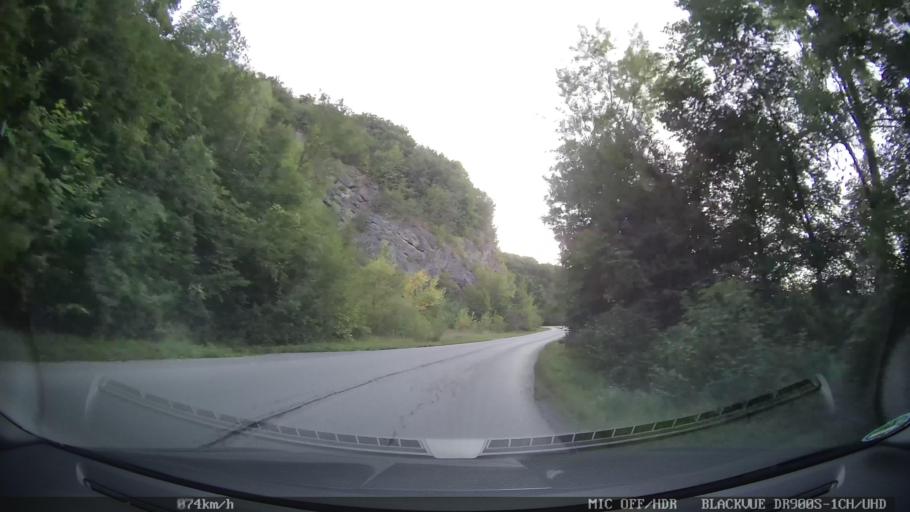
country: HR
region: Karlovacka
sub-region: Grad Ogulin
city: Ogulin
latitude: 45.2689
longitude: 15.1826
